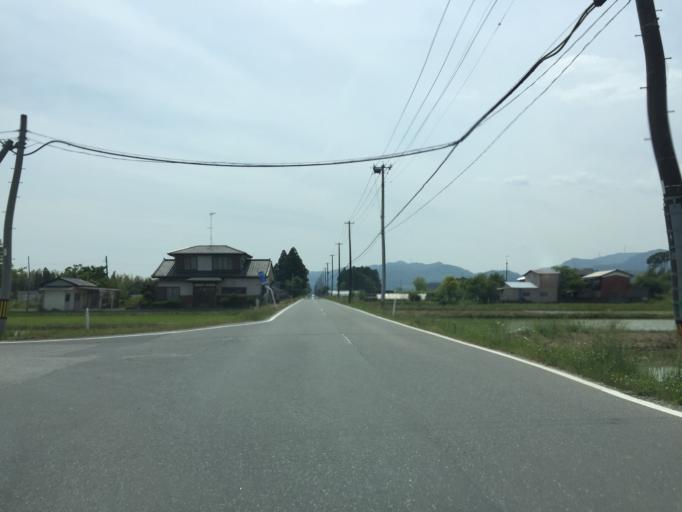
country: JP
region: Fukushima
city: Namie
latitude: 37.6237
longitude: 140.9351
